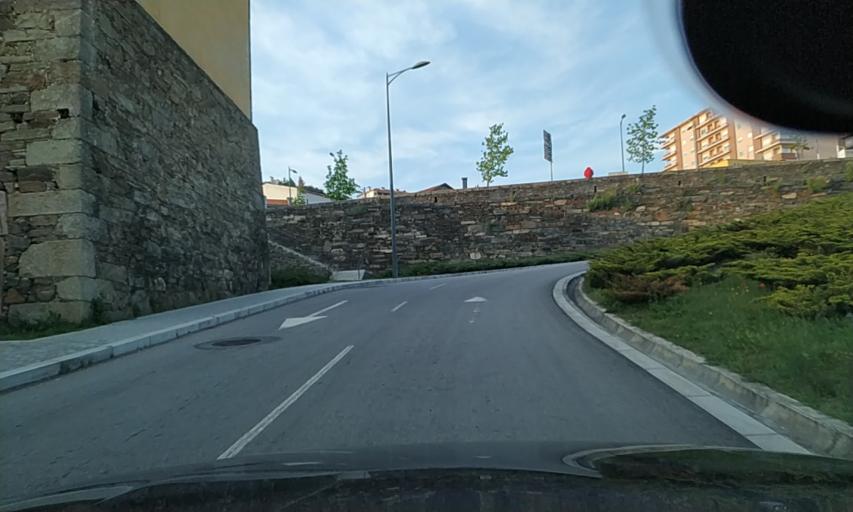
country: PT
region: Vila Real
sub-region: Peso da Regua
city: Peso da Regua
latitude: 41.1561
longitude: -7.7804
